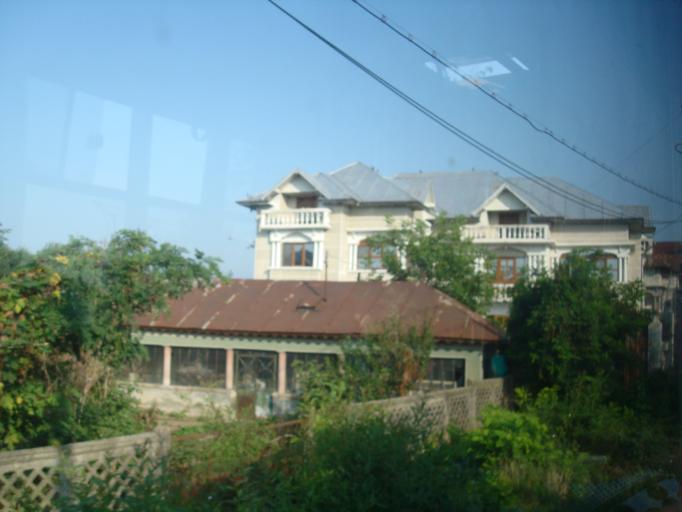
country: RO
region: Ilfov
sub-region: Comuna Vidra
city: Sintesti
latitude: 44.3111
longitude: 26.1110
